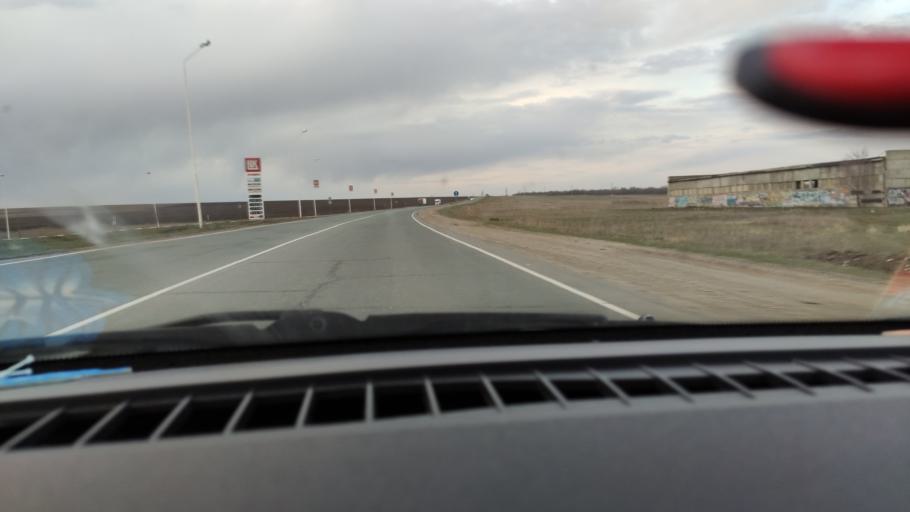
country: RU
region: Saratov
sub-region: Saratovskiy Rayon
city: Saratov
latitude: 51.7390
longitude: 46.0419
